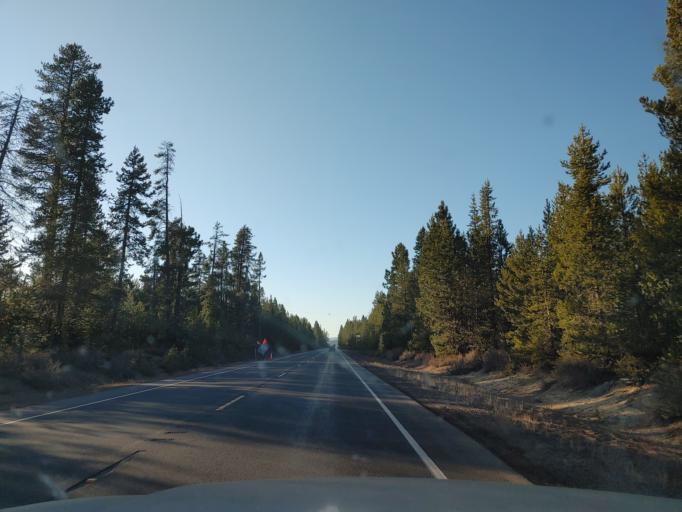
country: US
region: Oregon
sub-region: Deschutes County
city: La Pine
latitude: 43.3870
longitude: -121.8076
